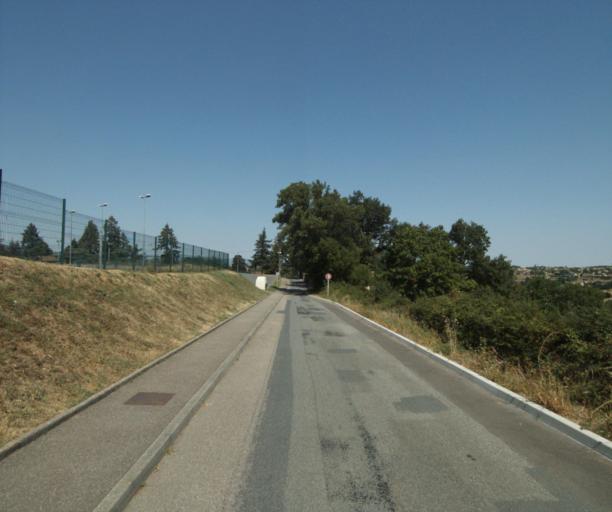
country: FR
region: Rhone-Alpes
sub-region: Departement du Rhone
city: Saint-Pierre-la-Palud
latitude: 45.7938
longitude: 4.6142
